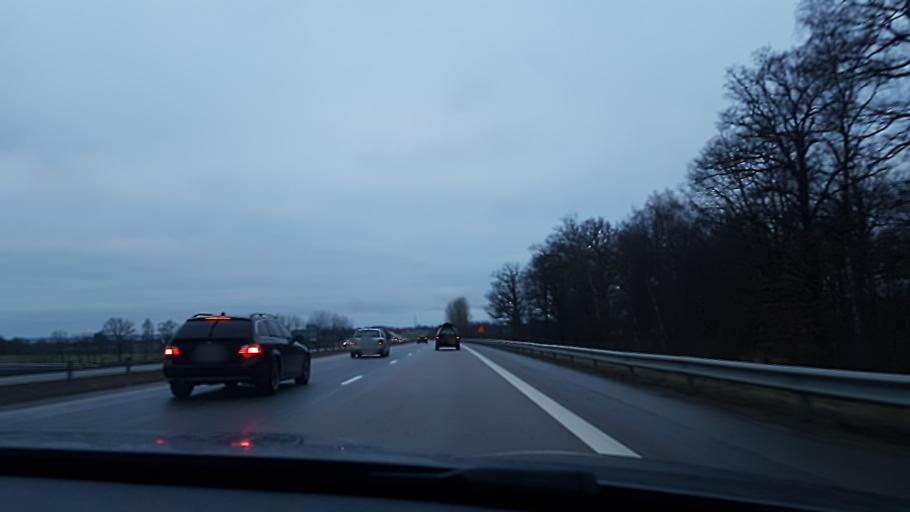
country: SE
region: Skane
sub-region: Astorps Kommun
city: Kvidinge
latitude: 56.2031
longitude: 13.0874
